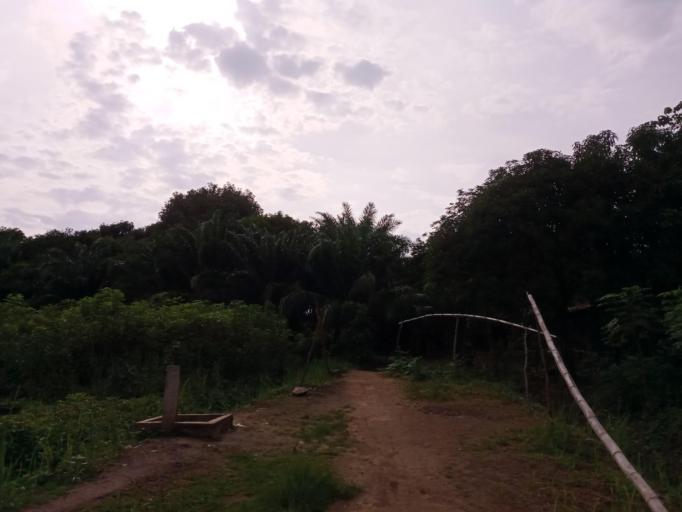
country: SL
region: Northern Province
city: Bumbuna
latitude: 9.0504
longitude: -11.7571
